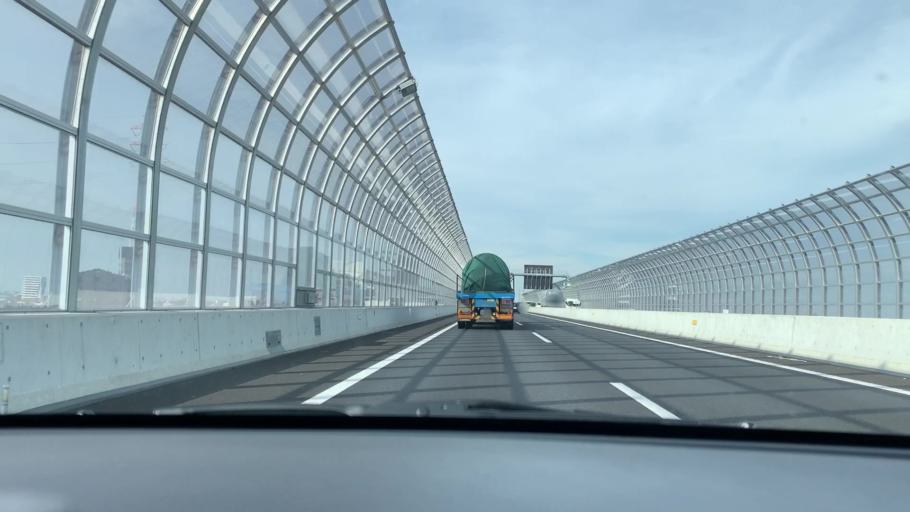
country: JP
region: Chiba
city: Matsudo
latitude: 35.7727
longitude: 139.8915
